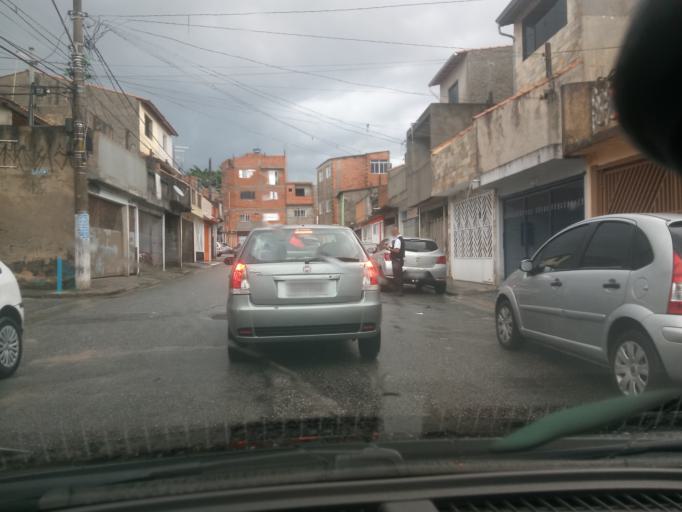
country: BR
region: Sao Paulo
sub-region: Sao Bernardo Do Campo
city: Sao Bernardo do Campo
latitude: -23.7028
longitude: -46.5578
